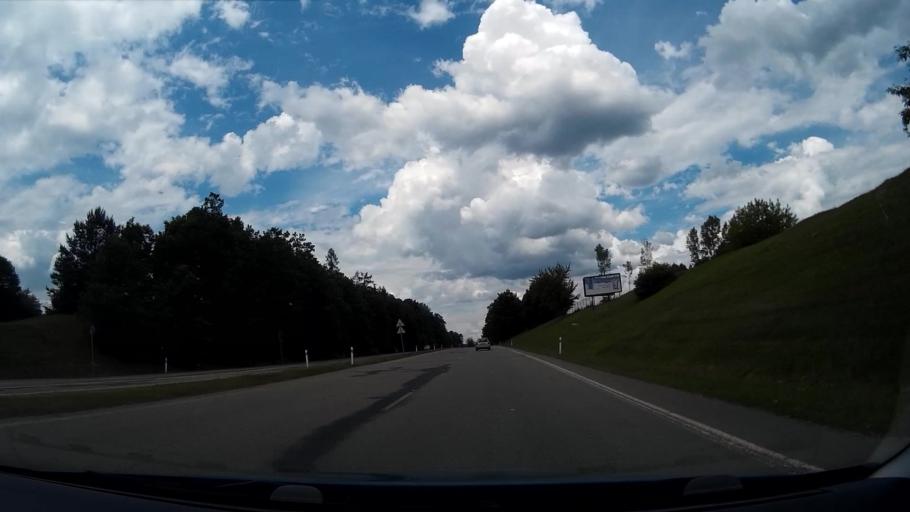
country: CZ
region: South Moravian
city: Troubsko
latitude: 49.2160
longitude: 16.5218
